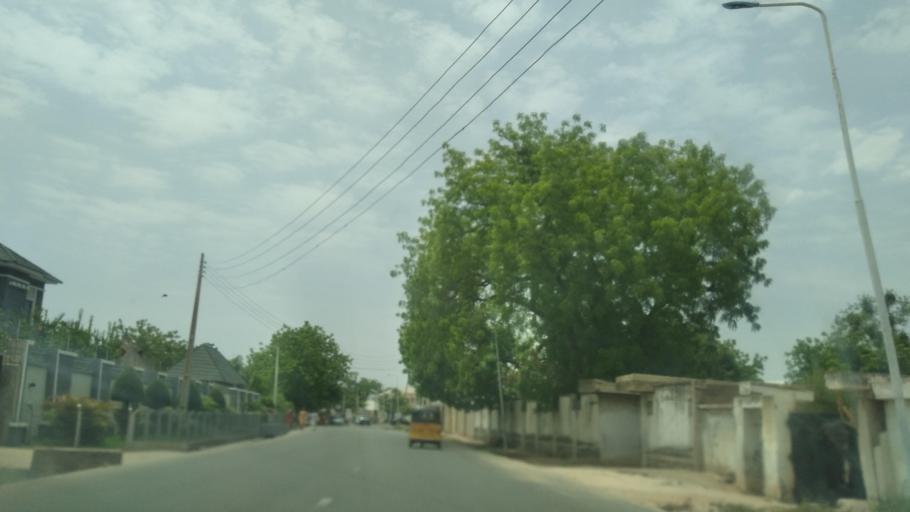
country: NG
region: Borno
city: Maiduguri
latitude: 11.8073
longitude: 13.1606
